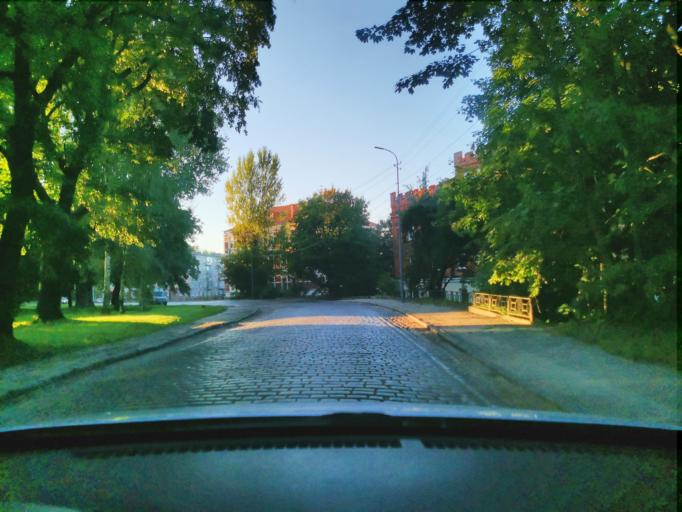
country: RU
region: Kaliningrad
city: Chernyakhovsk
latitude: 54.6388
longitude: 21.8090
